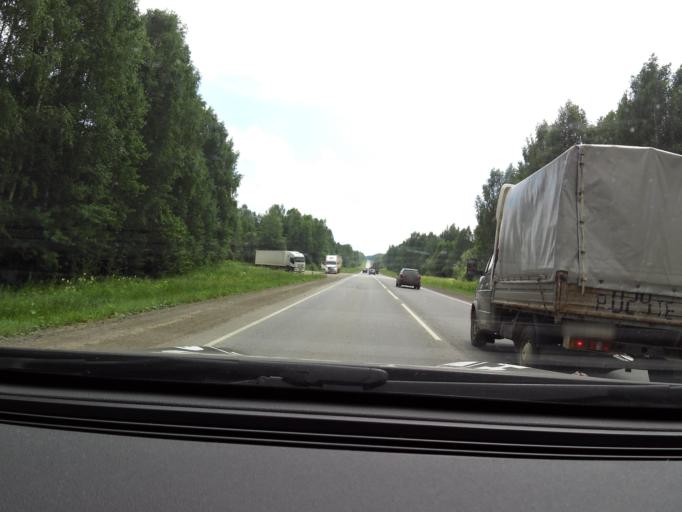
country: RU
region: Perm
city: Kukushtan
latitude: 57.5680
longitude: 56.5662
